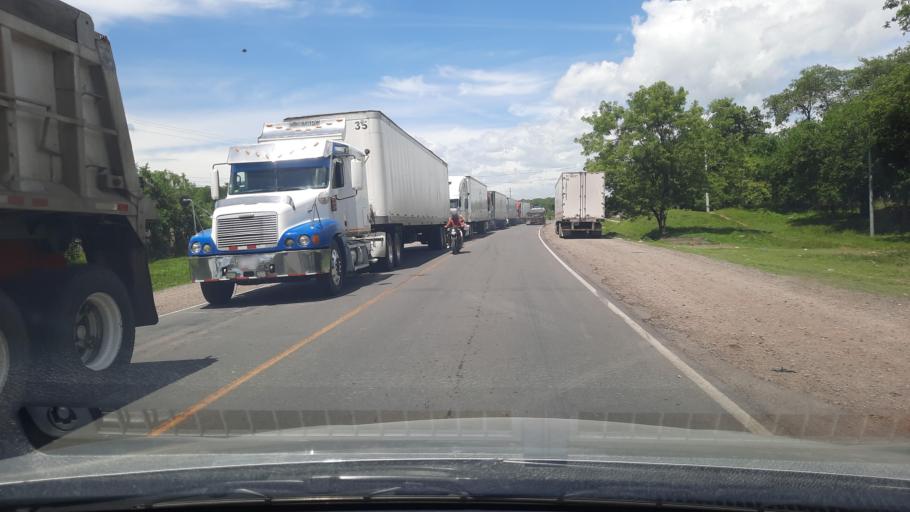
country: NI
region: Chinandega
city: Somotillo
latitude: 13.0593
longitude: -86.9302
